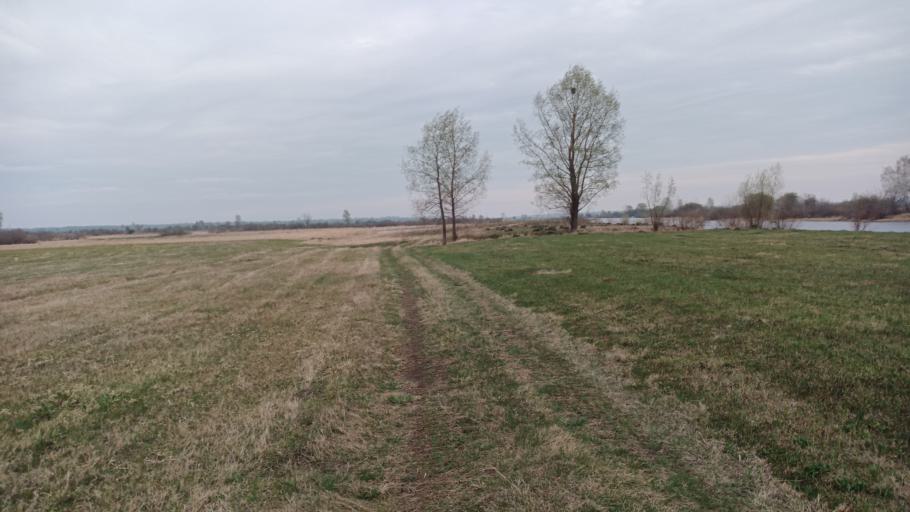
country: RU
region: Altai Krai
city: Yuzhnyy
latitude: 53.2232
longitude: 83.7370
